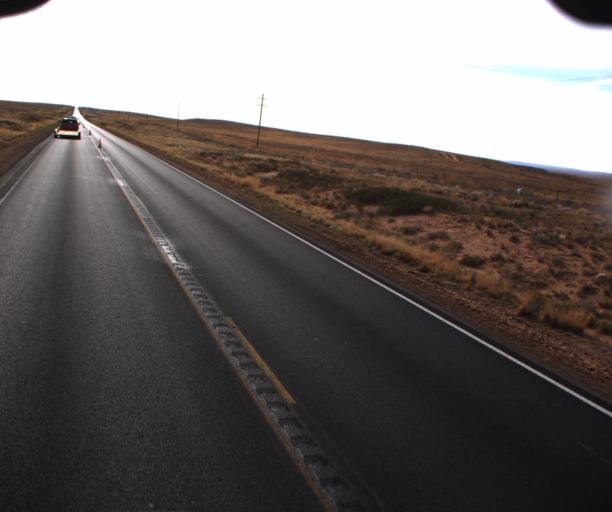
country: US
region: Arizona
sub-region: Apache County
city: Chinle
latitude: 36.0830
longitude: -109.6182
